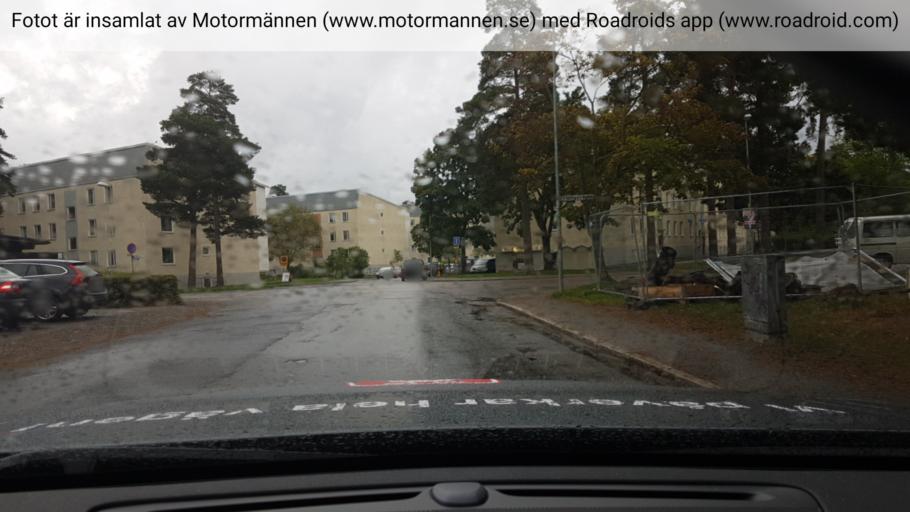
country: SE
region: Stockholm
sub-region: Haninge Kommun
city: Haninge
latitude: 59.1711
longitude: 18.1457
